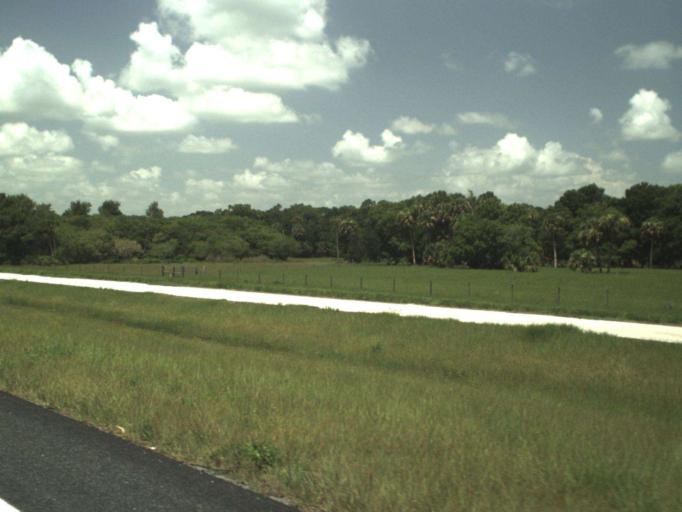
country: US
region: Florida
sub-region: Okeechobee County
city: Taylor Creek
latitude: 27.3385
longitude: -80.6463
